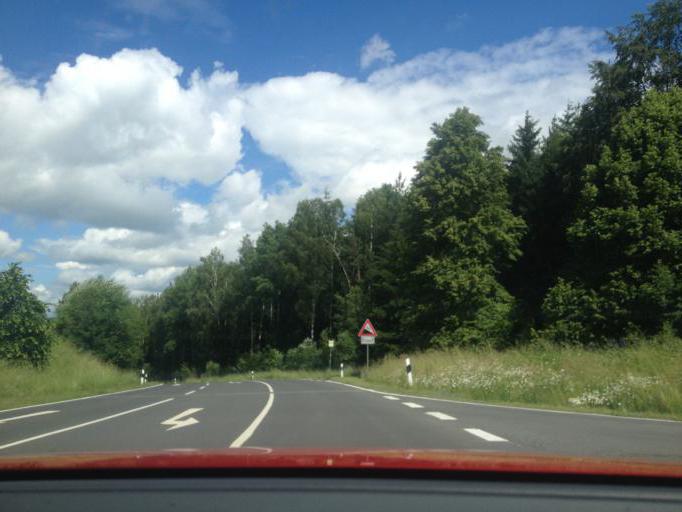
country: DE
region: Bavaria
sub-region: Upper Franconia
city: Arzberg
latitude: 50.0455
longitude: 12.2003
